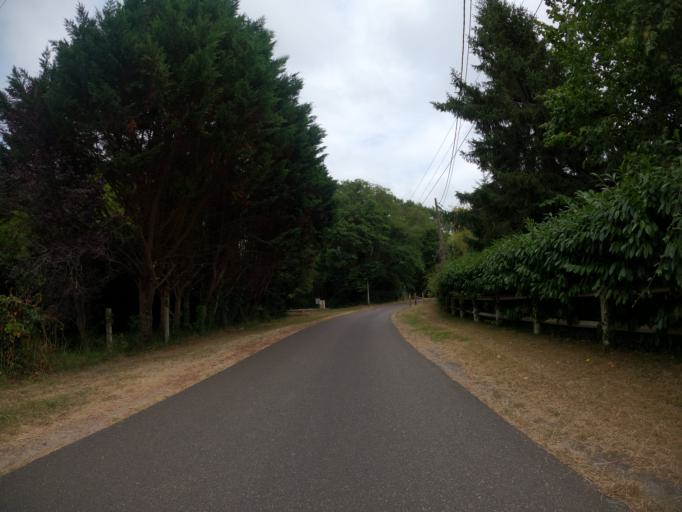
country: FR
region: Aquitaine
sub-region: Departement des Landes
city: Leon
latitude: 43.8852
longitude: -1.3051
